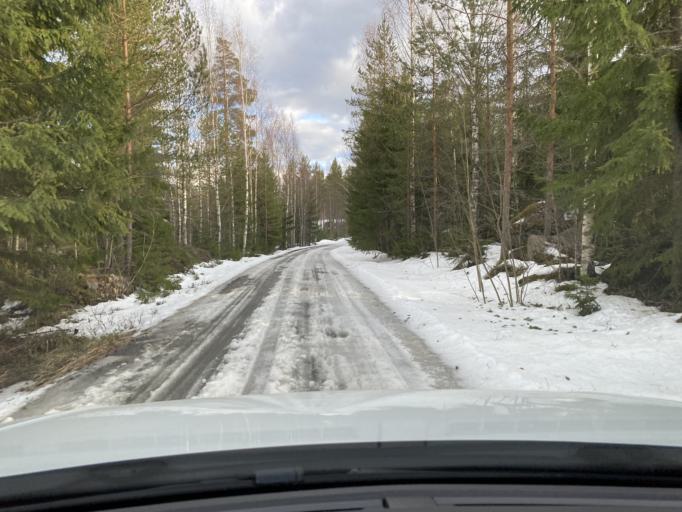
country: FI
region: Pirkanmaa
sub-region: Lounais-Pirkanmaa
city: Mouhijaervi
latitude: 61.4329
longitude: 22.9875
